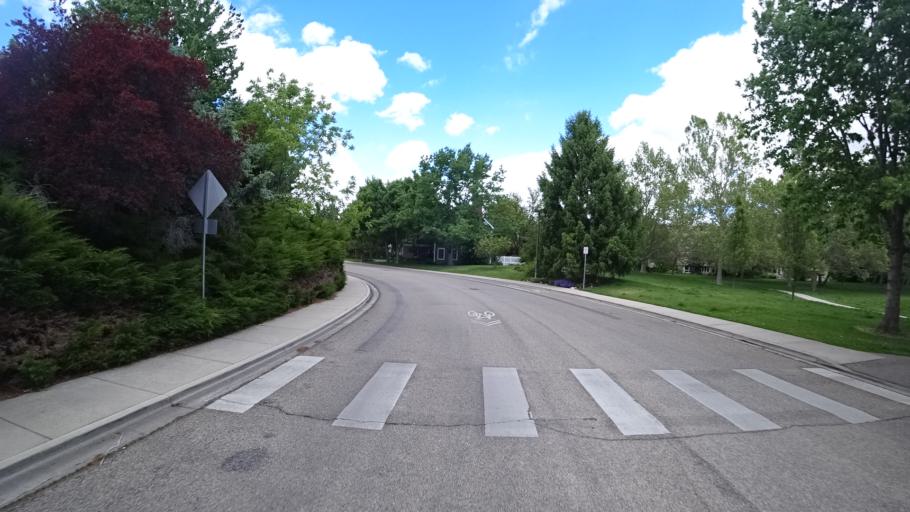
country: US
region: Idaho
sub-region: Ada County
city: Boise
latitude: 43.5831
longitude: -116.1658
